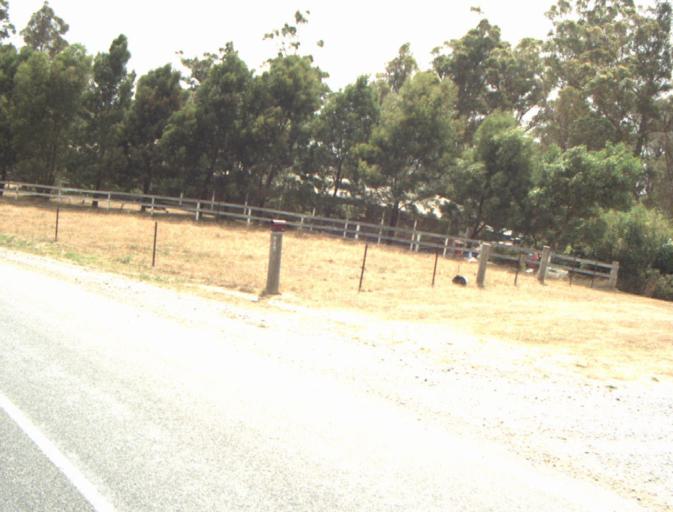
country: AU
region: Tasmania
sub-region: Launceston
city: Mayfield
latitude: -41.2021
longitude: 147.2181
